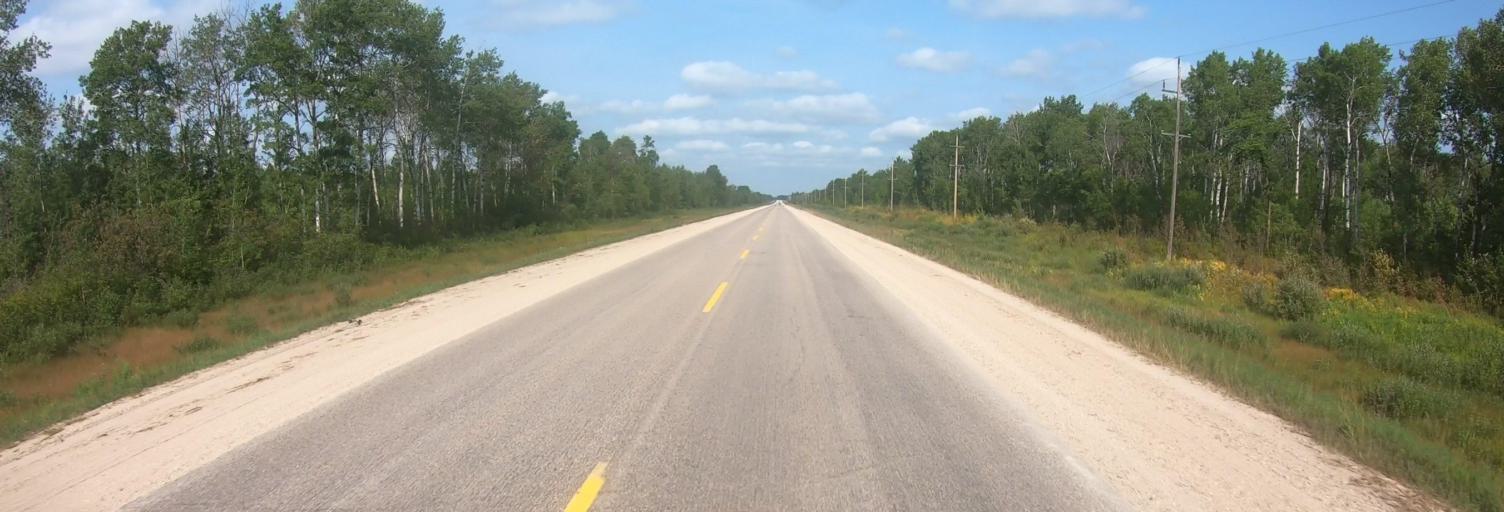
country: CA
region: Manitoba
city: La Broquerie
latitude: 49.1996
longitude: -96.2704
